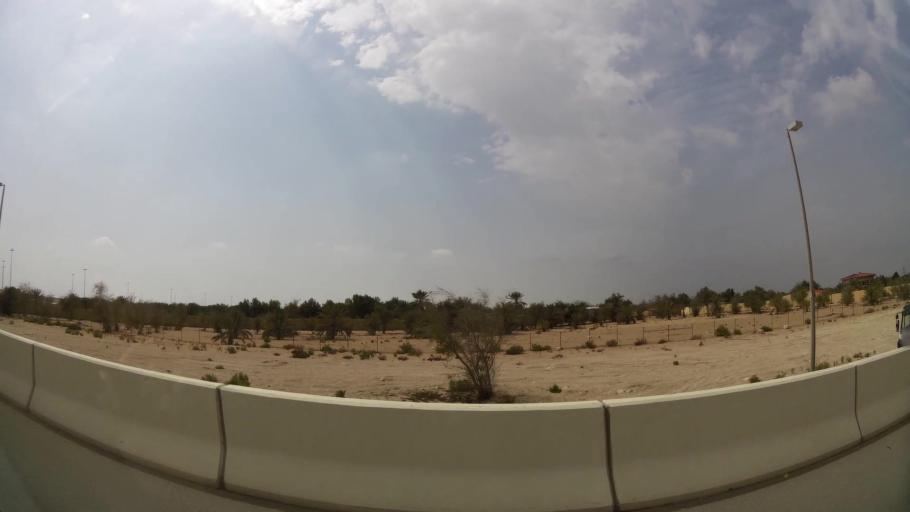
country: AE
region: Abu Dhabi
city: Abu Dhabi
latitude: 24.5129
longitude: 54.6615
